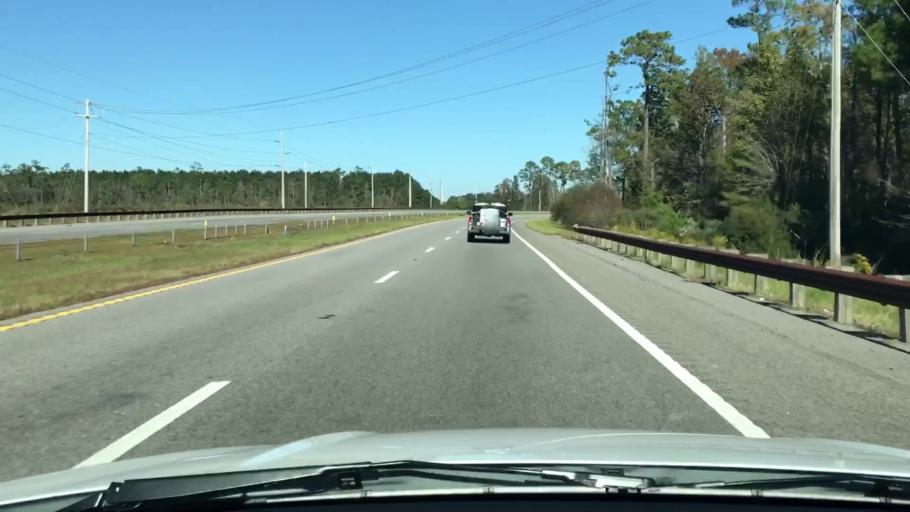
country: US
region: South Carolina
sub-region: Colleton County
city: Walterboro
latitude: 32.7578
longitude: -80.5294
